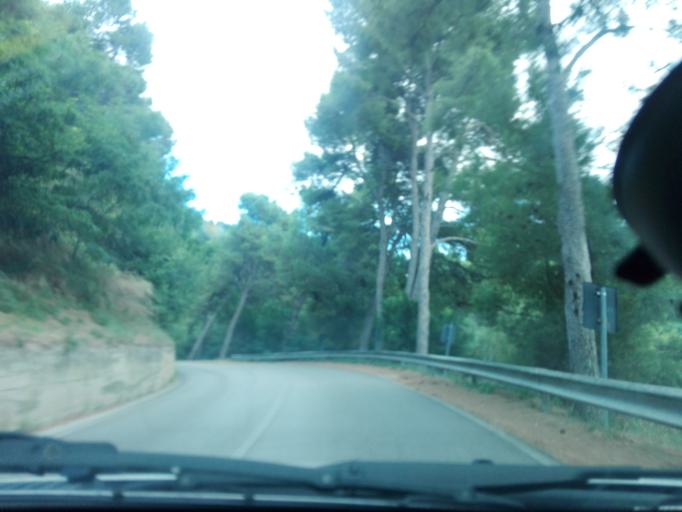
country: IT
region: Abruzzo
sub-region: Provincia di Pescara
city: Montesilvano Marina
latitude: 42.4944
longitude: 14.1439
